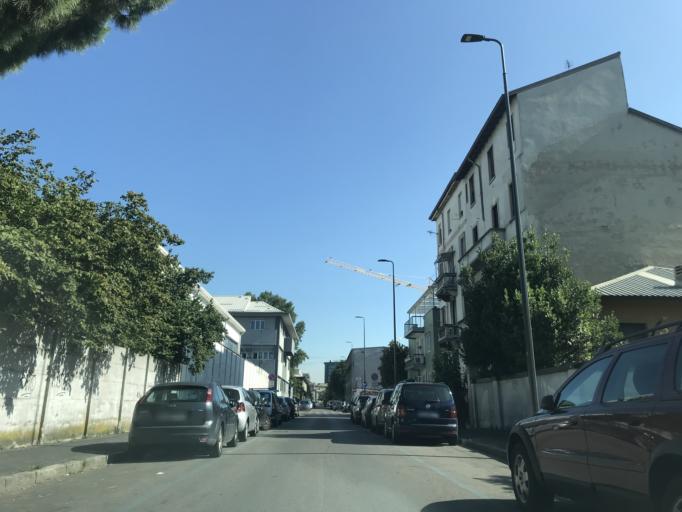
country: IT
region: Lombardy
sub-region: Citta metropolitana di Milano
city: Sesto San Giovanni
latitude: 45.5178
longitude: 9.2284
